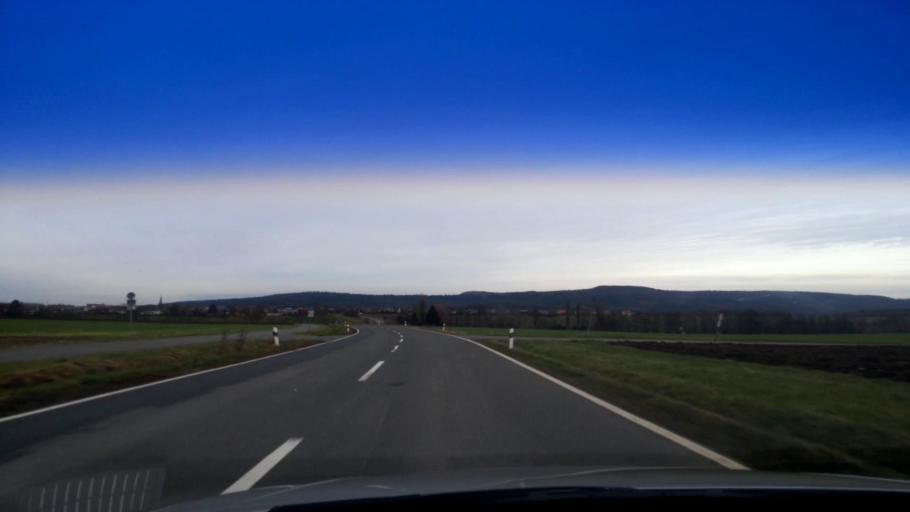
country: DE
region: Bavaria
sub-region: Upper Franconia
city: Litzendorf
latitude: 49.9005
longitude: 11.0099
